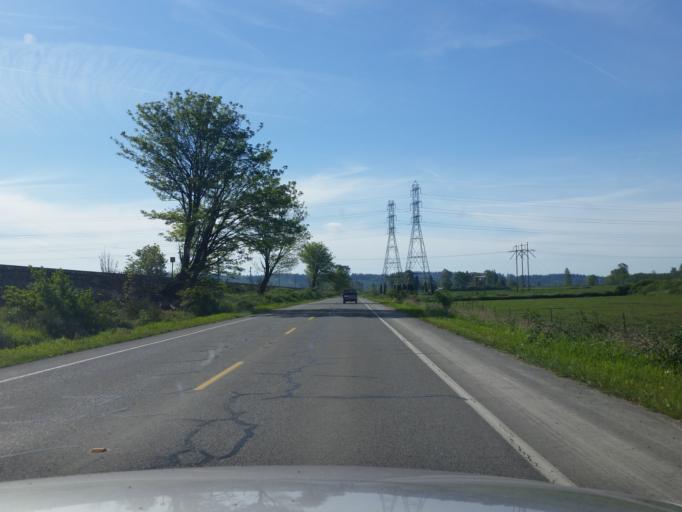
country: US
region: Washington
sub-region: Snohomish County
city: Snohomish
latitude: 47.9165
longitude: -122.1329
